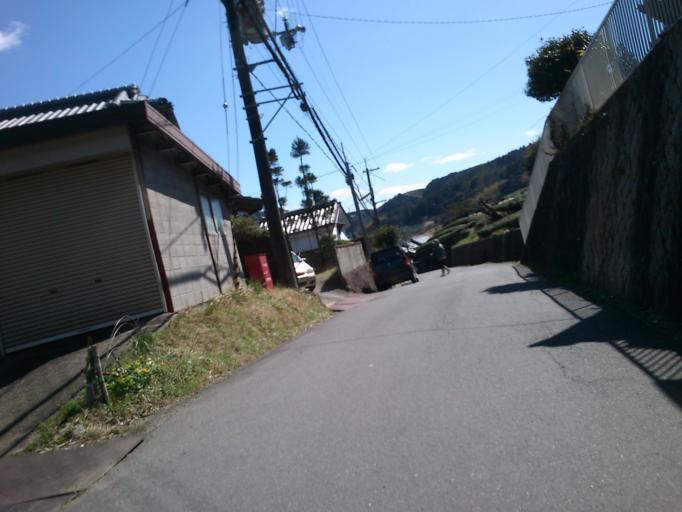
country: JP
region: Kyoto
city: Uji
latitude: 34.7923
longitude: 135.9040
